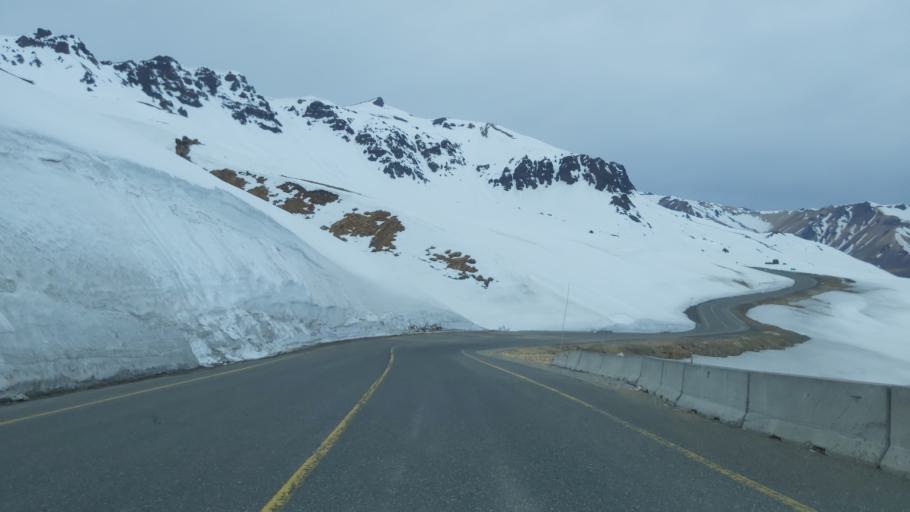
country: CL
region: Maule
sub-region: Provincia de Linares
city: Colbun
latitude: -36.0142
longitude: -70.4890
